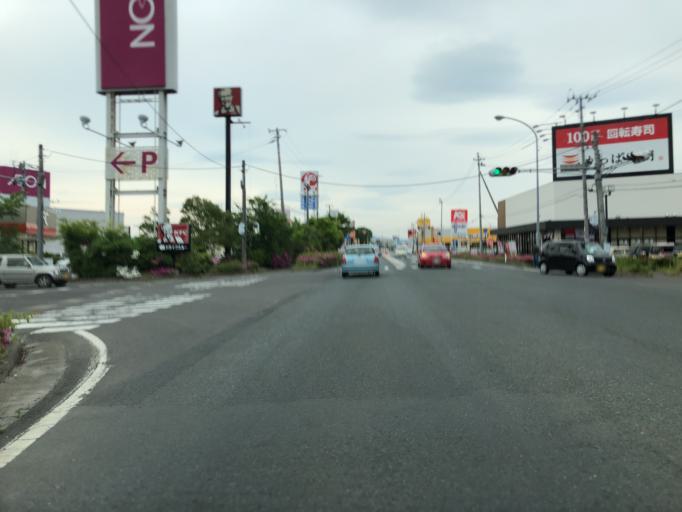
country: JP
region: Miyagi
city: Marumori
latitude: 37.7874
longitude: 140.9324
